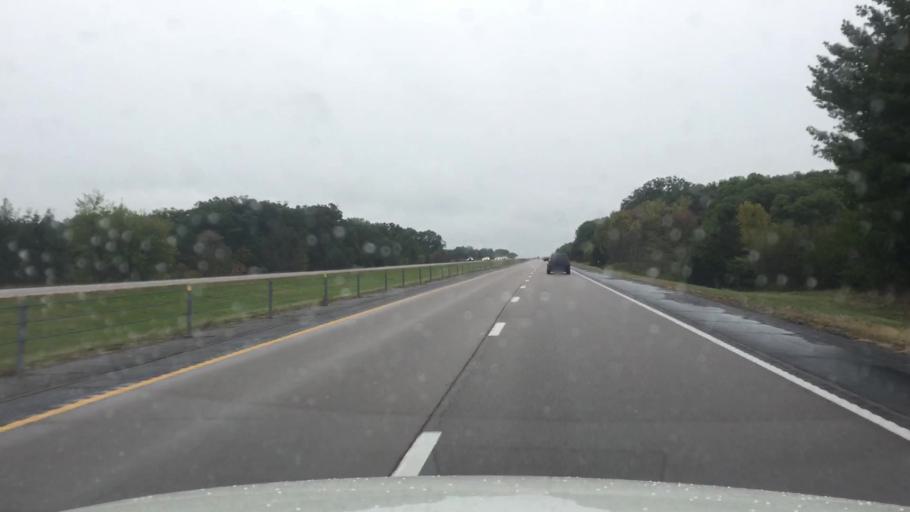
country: US
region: Missouri
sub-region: Boone County
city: Ashland
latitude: 38.7277
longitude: -92.2543
